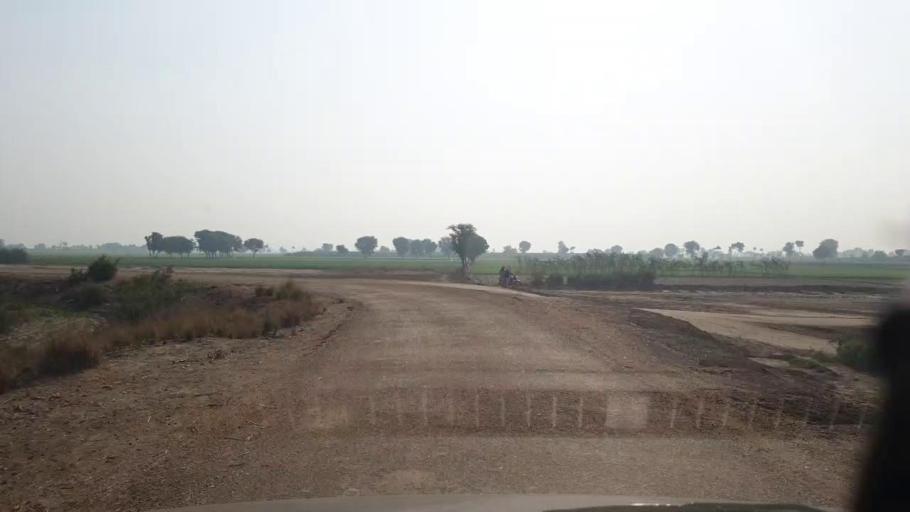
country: PK
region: Sindh
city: Shahdadpur
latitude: 26.0403
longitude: 68.4921
